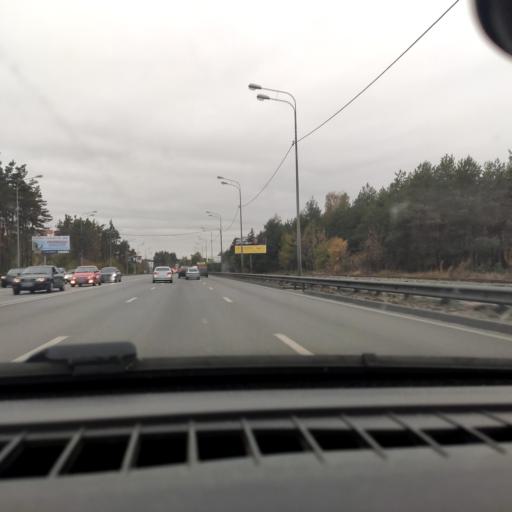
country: RU
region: Voronezj
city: Podgornoye
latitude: 51.6906
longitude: 39.1243
